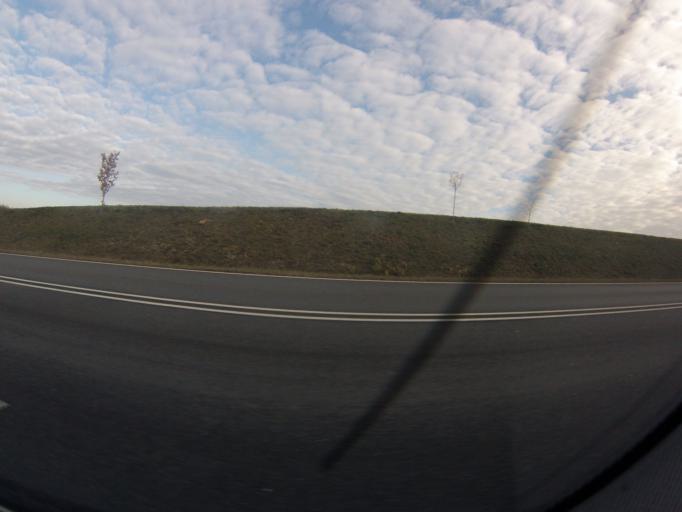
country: DE
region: Thuringia
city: Gossnitz
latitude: 50.8986
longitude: 12.4438
